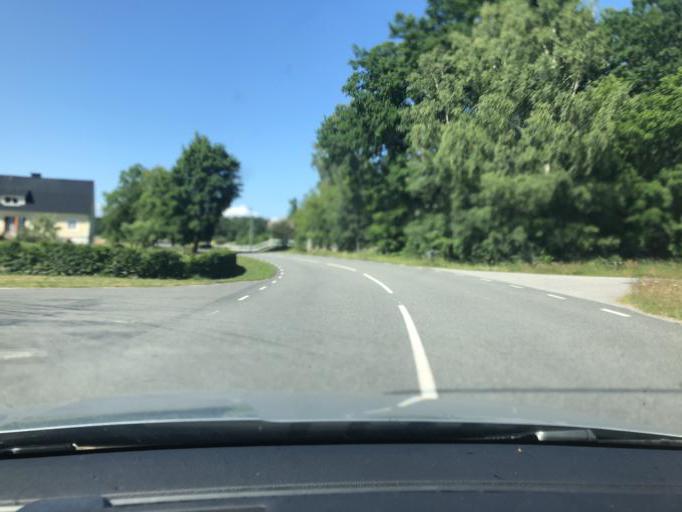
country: SE
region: Blekinge
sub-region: Karlshamns Kommun
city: Morrum
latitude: 56.1673
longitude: 14.6816
